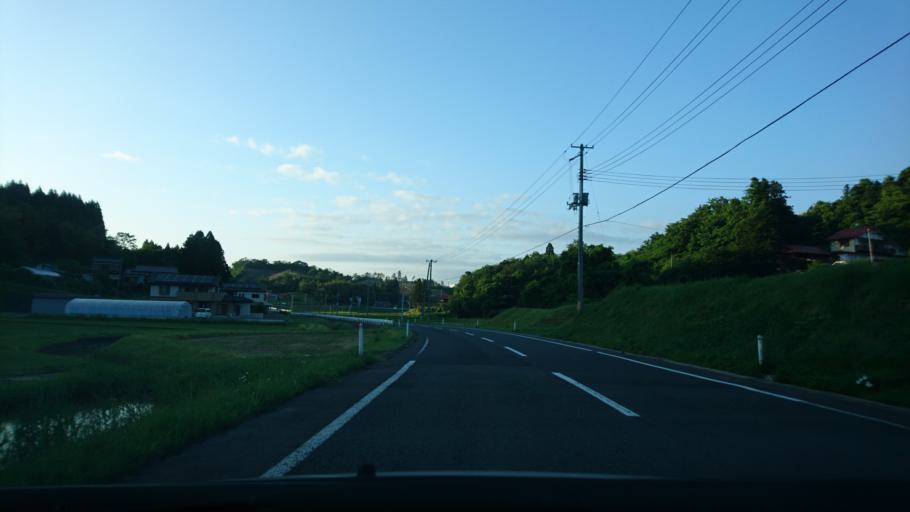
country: JP
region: Iwate
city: Ichinoseki
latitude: 38.8953
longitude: 141.1594
